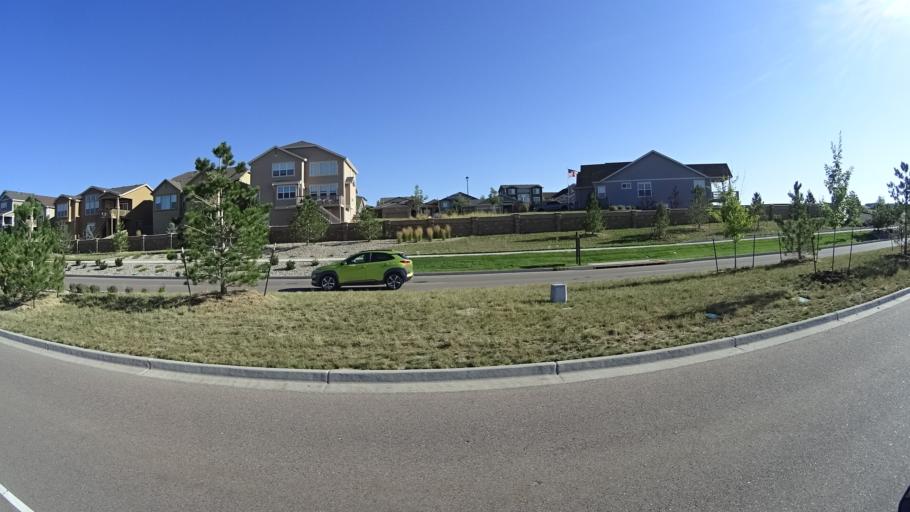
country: US
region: Colorado
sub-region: El Paso County
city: Black Forest
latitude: 38.9710
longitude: -104.7295
